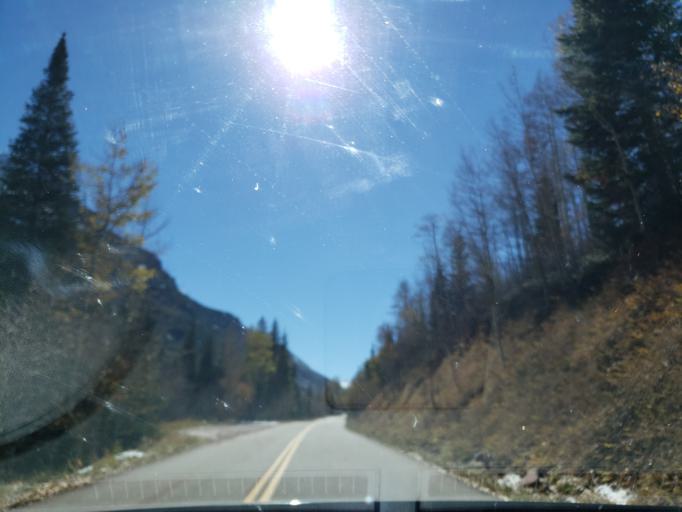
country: US
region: Colorado
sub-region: Pitkin County
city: Snowmass Village
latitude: 39.1403
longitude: -106.8980
